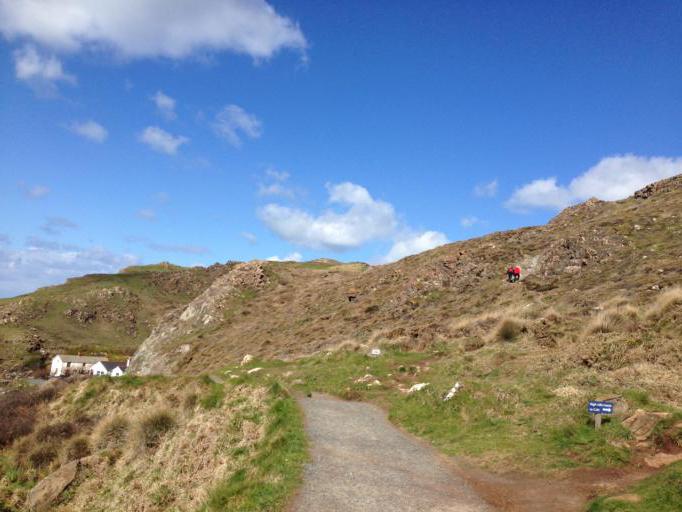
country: GB
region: England
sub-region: Cornwall
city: Landewednack
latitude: 49.9752
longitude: -5.2287
